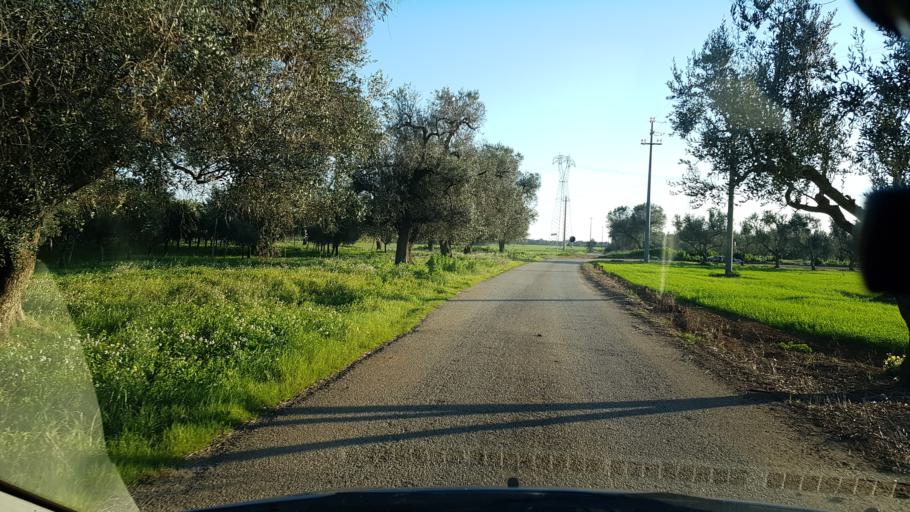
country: IT
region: Apulia
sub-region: Provincia di Brindisi
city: Mesagne
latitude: 40.5571
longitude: 17.8643
